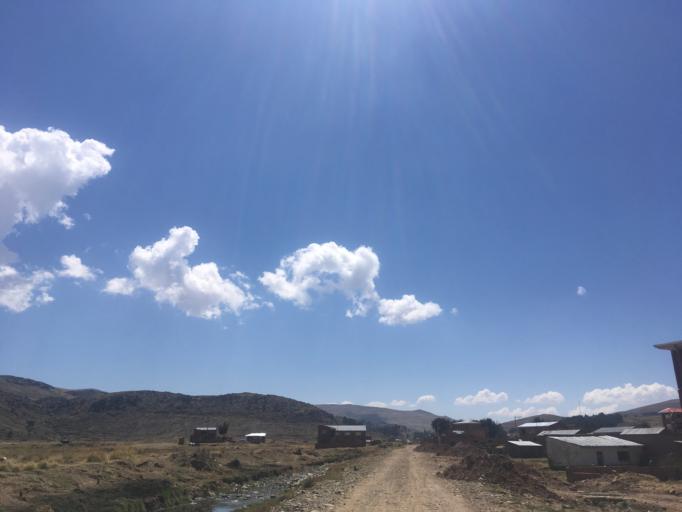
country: BO
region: La Paz
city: Huatajata
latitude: -16.1889
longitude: -68.7455
